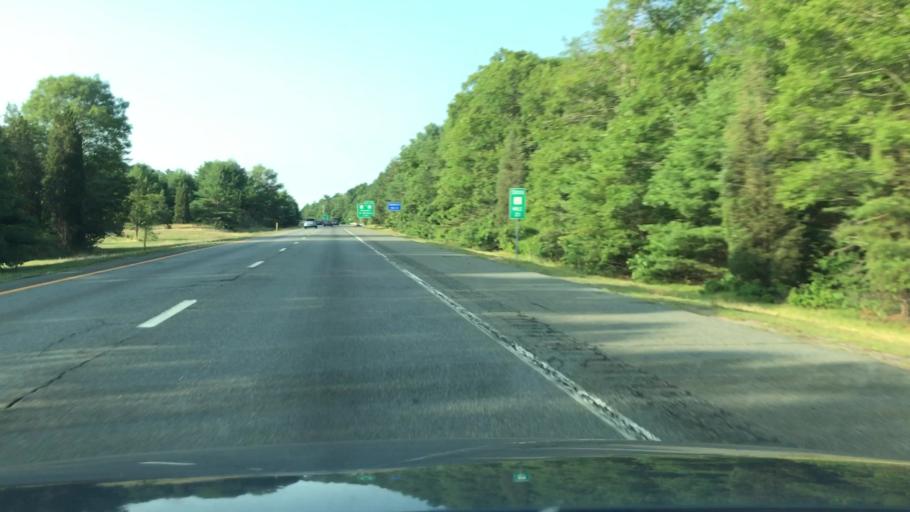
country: US
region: Massachusetts
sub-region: Plymouth County
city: Kingston
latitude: 42.0335
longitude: -70.7251
